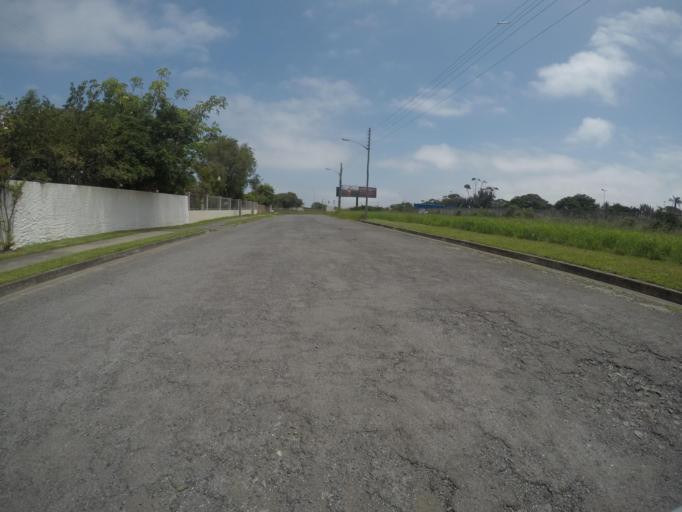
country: ZA
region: Eastern Cape
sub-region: Buffalo City Metropolitan Municipality
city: East London
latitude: -32.9979
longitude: 27.9168
